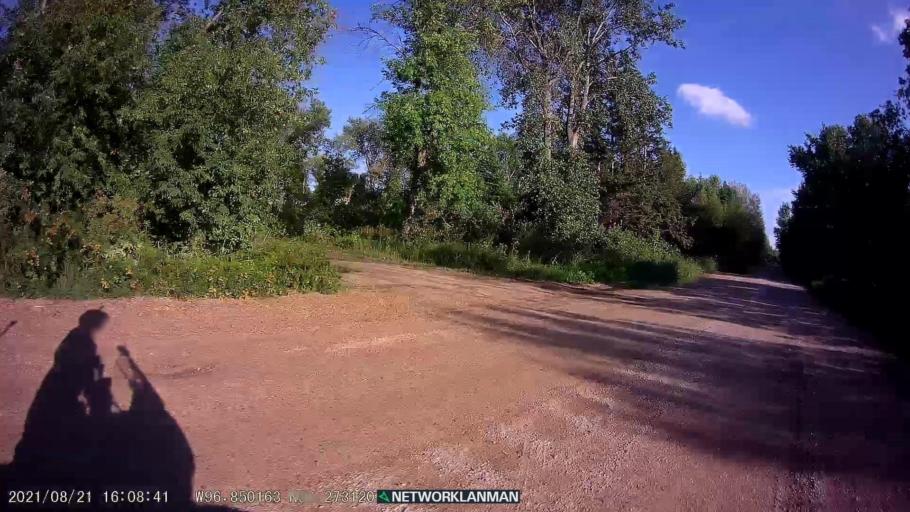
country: CA
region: Manitoba
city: Selkirk
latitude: 50.2732
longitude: -96.8502
